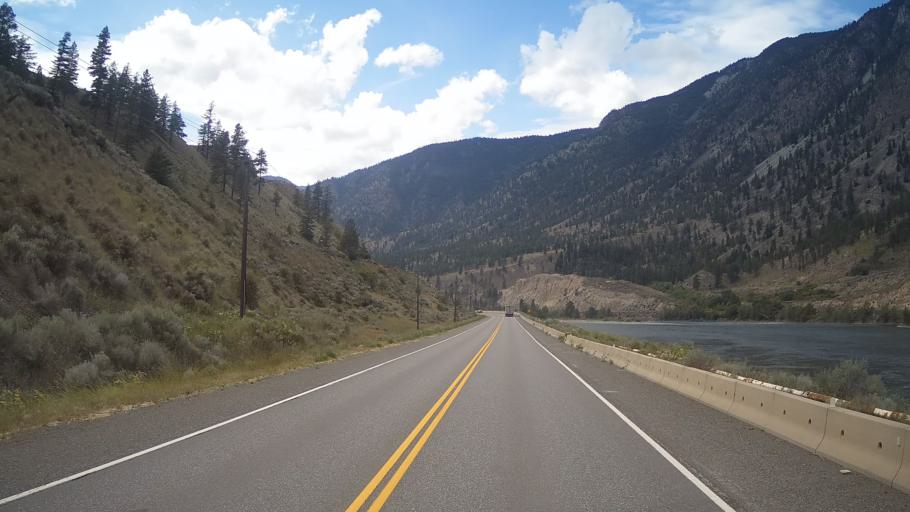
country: CA
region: British Columbia
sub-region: Thompson-Nicola Regional District
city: Ashcroft
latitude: 50.4078
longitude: -121.3683
